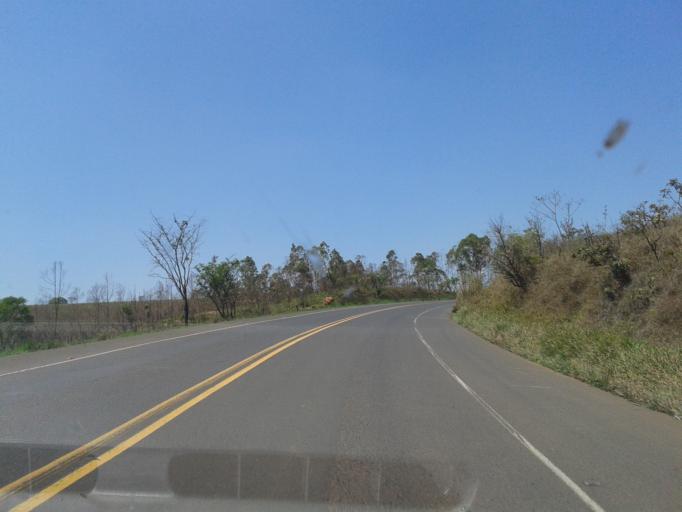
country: BR
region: Minas Gerais
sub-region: Araxa
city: Araxa
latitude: -19.4608
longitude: -47.1703
